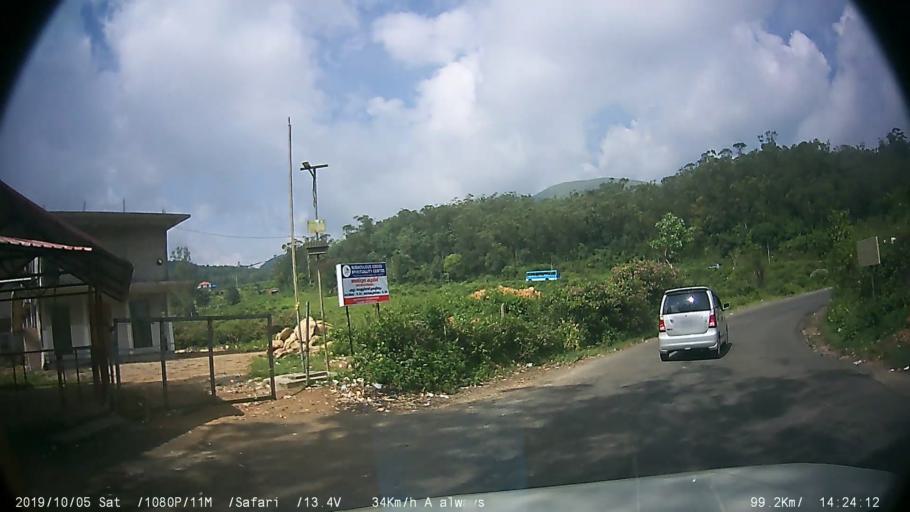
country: IN
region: Kerala
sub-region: Kottayam
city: Erattupetta
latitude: 9.5938
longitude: 76.9689
